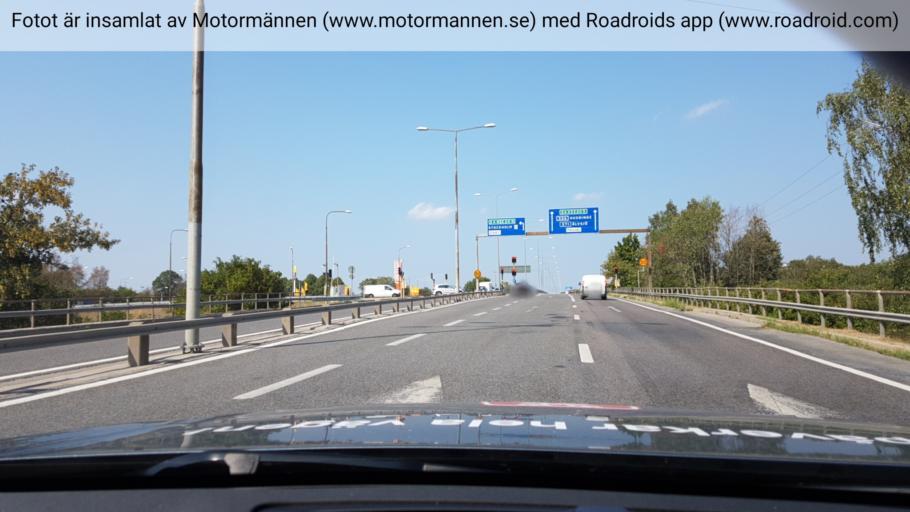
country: SE
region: Stockholm
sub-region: Stockholms Kommun
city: Arsta
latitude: 59.2709
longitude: 18.0165
